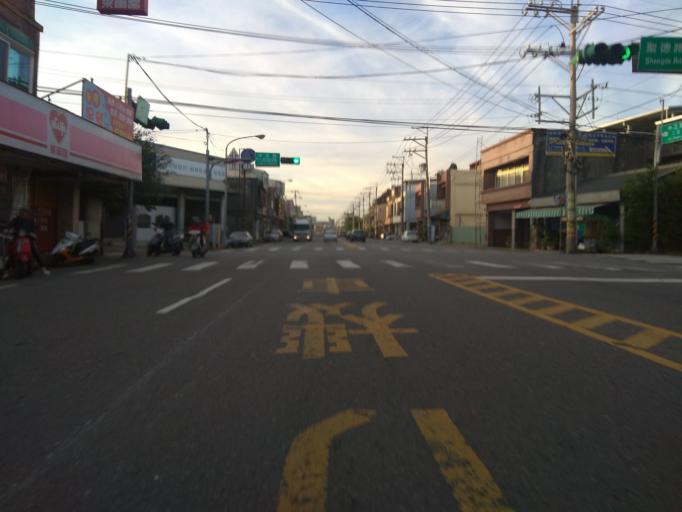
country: TW
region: Taiwan
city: Taoyuan City
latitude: 24.9794
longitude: 121.1936
